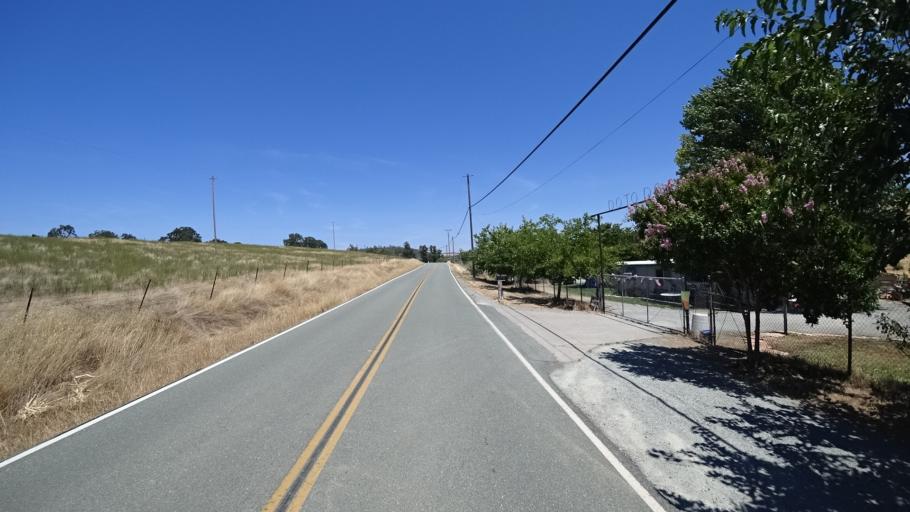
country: US
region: California
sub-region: Calaveras County
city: Valley Springs
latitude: 38.2236
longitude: -120.8220
